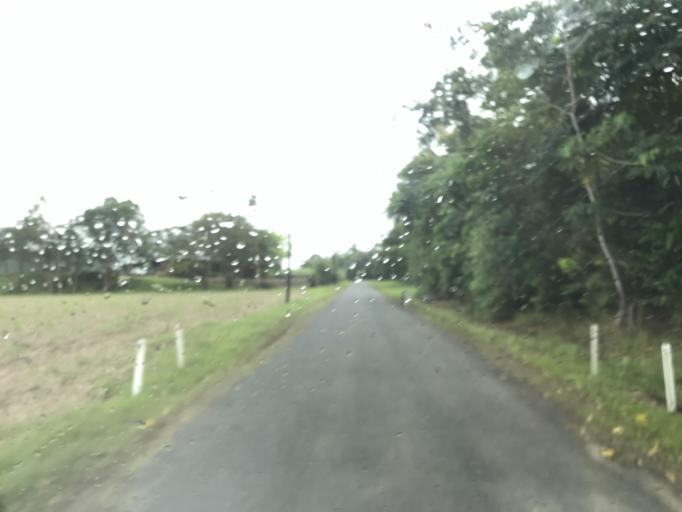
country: AU
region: Queensland
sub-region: Cassowary Coast
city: Innisfail
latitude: -17.4937
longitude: 145.9882
